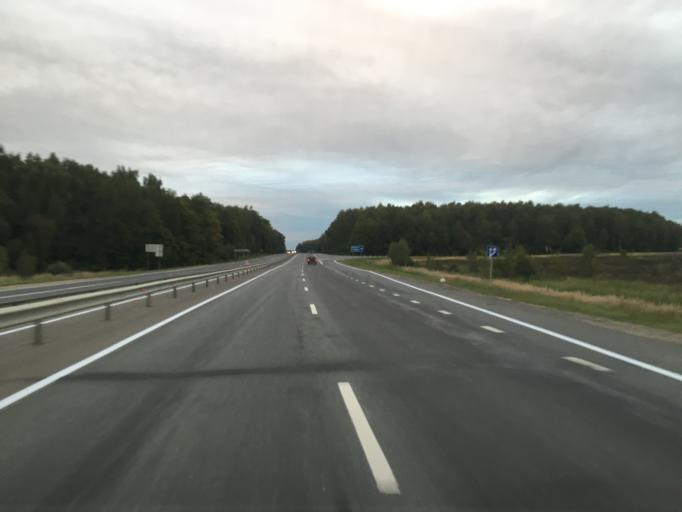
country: RU
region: Kaluga
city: Kaluga
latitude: 54.5738
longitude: 36.3347
